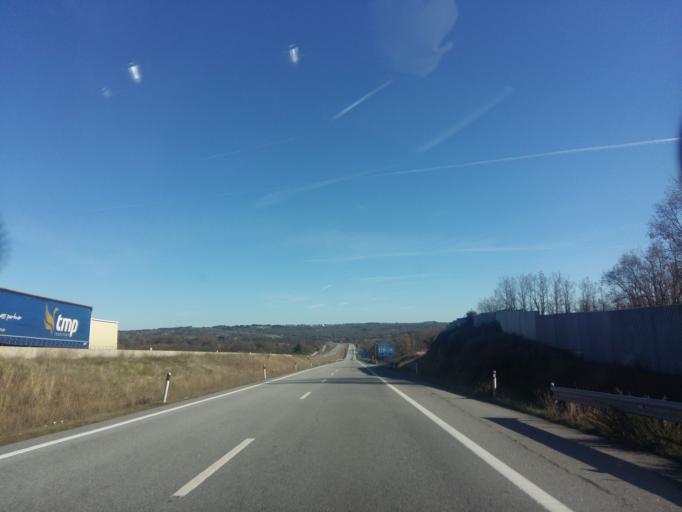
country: PT
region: Guarda
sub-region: Pinhel
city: Pinhel
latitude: 40.6043
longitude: -7.0619
